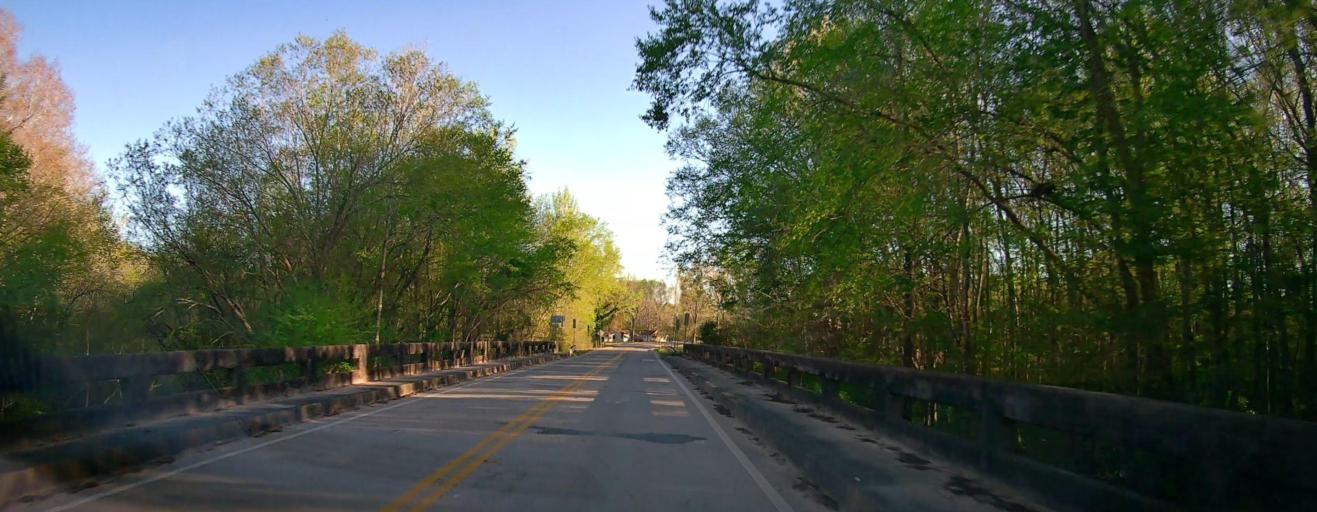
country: US
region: Georgia
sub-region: Wilkinson County
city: Irwinton
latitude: 32.8313
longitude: -83.0792
